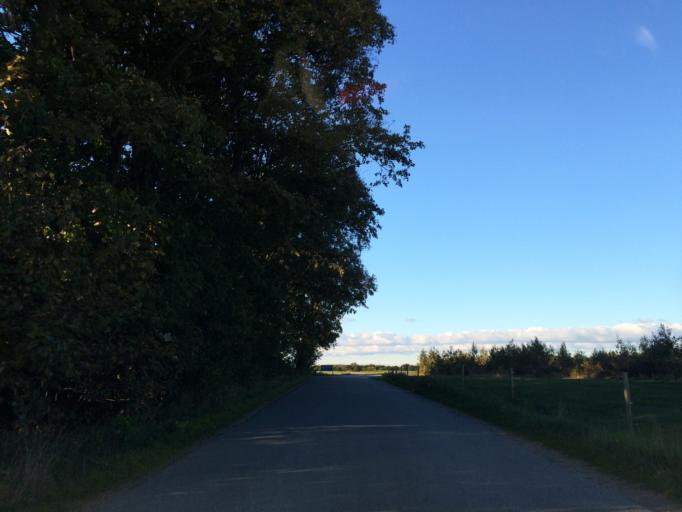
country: DK
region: Central Jutland
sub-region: Silkeborg Kommune
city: Svejbaek
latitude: 56.1788
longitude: 9.6925
